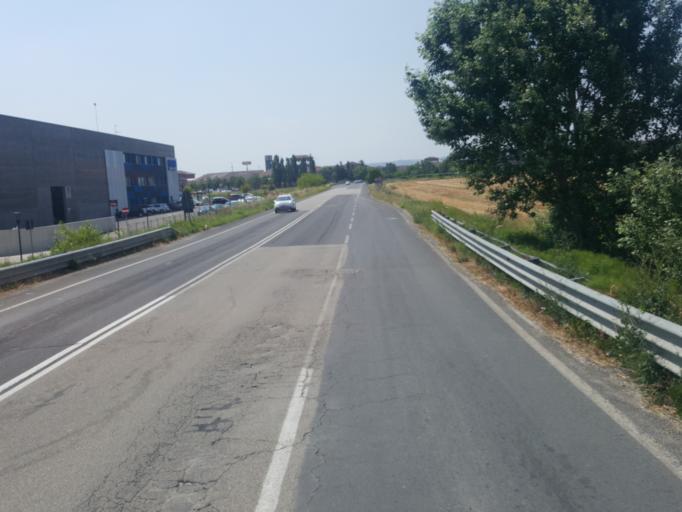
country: IT
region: Emilia-Romagna
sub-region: Provincia di Bologna
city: Castel San Pietro Terme
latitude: 44.4394
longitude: 11.6062
